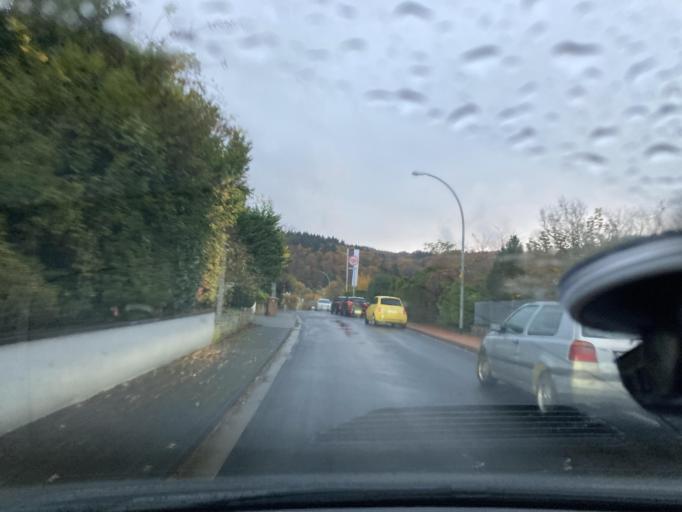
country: DE
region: Hesse
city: Kelkheim (Taunus)
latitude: 50.1360
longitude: 8.4395
